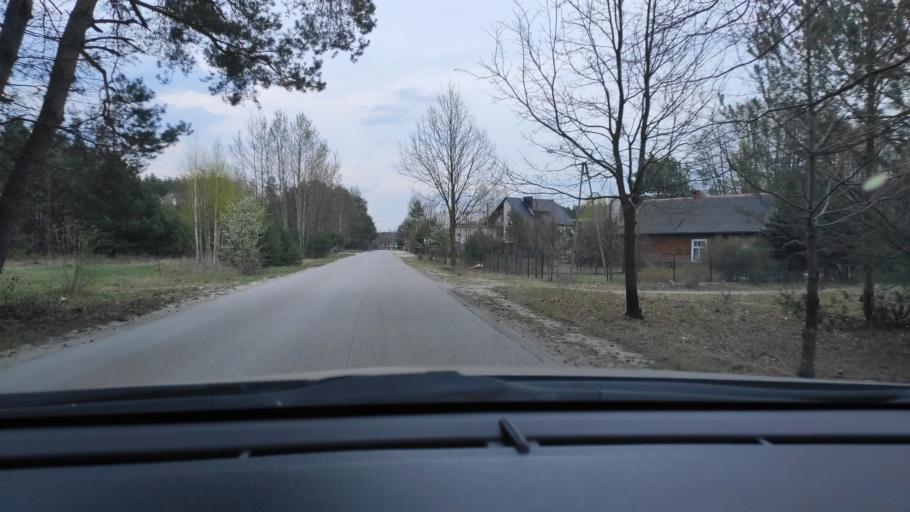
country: PL
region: Masovian Voivodeship
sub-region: Powiat radomski
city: Pionki
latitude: 51.5390
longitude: 21.3968
